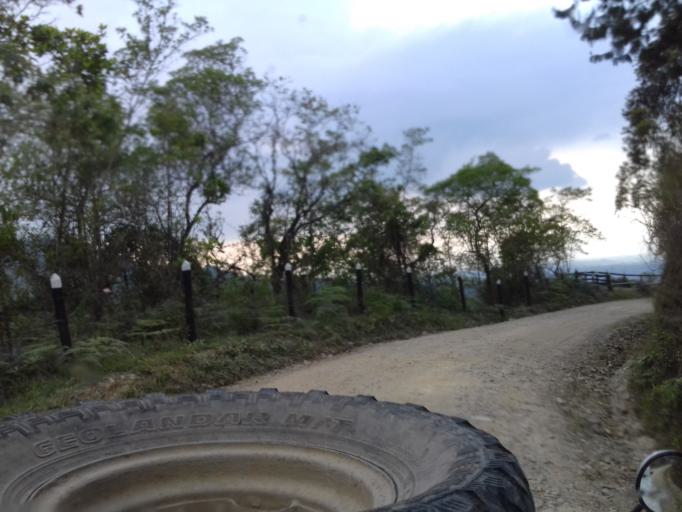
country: CO
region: Quindio
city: Salento
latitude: 4.6157
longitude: -75.5520
